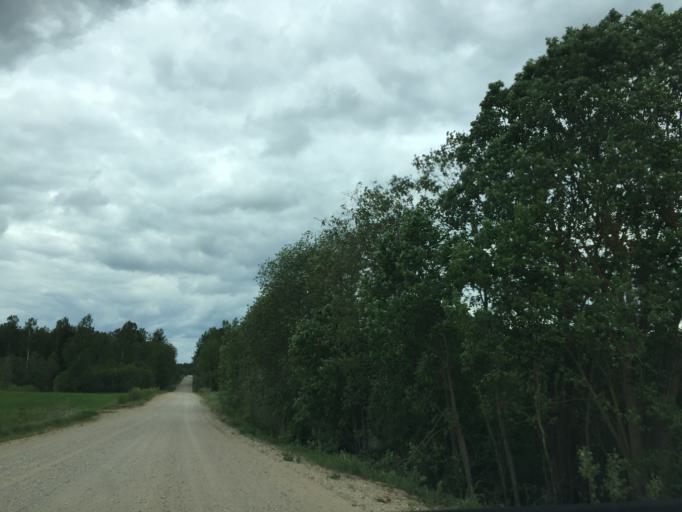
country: LV
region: Dagda
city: Dagda
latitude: 55.9873
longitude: 27.6070
